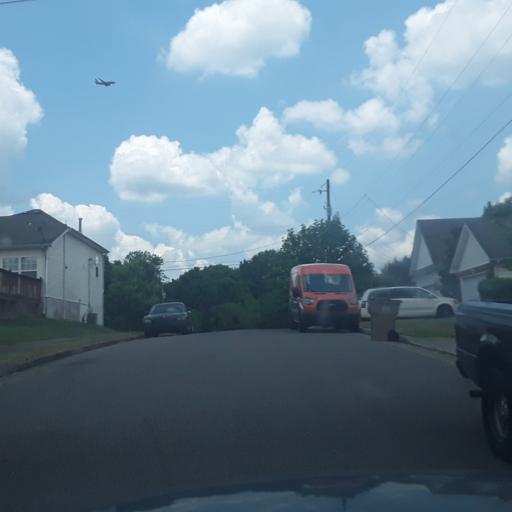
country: US
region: Tennessee
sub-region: Williamson County
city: Brentwood Estates
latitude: 36.0412
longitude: -86.7006
